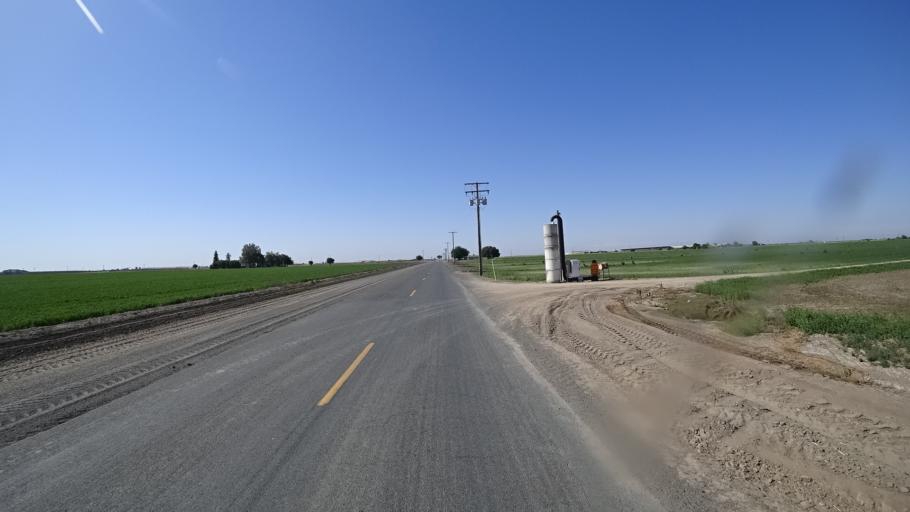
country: US
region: California
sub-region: Kings County
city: Home Garden
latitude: 36.2312
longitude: -119.5473
